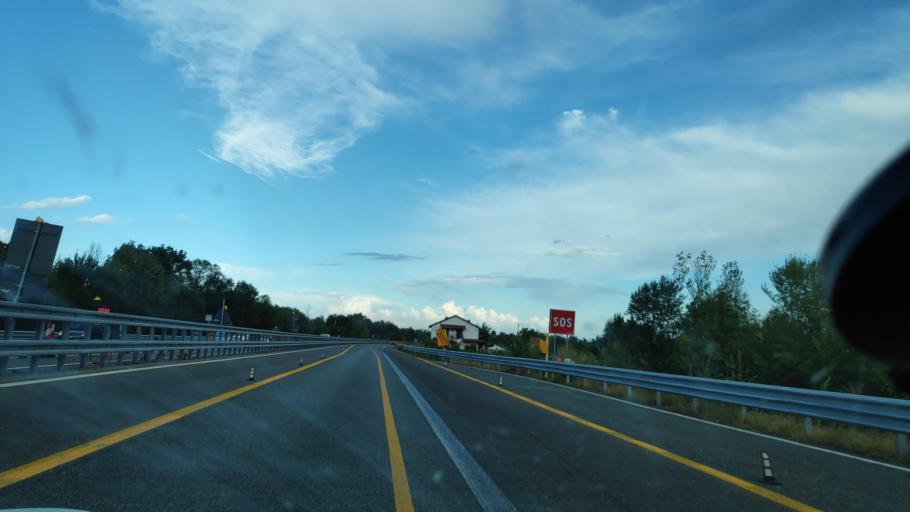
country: IT
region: Piedmont
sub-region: Provincia di Asti
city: Castello di Annone
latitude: 44.9090
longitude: 8.3230
